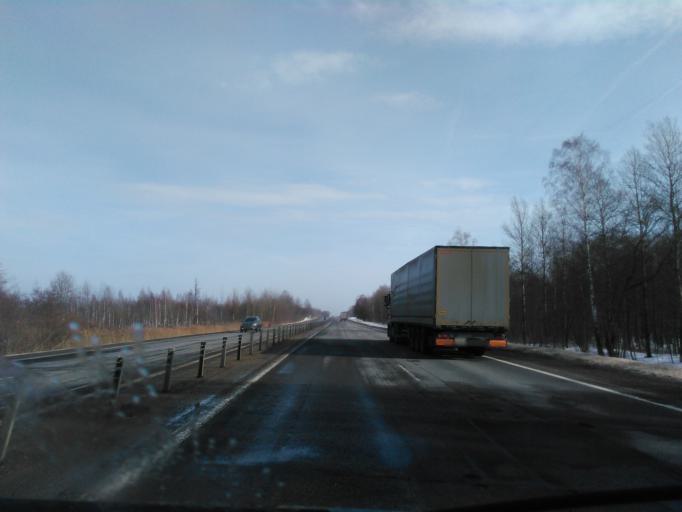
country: BY
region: Vitebsk
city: Dubrowna
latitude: 54.6838
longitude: 30.7890
